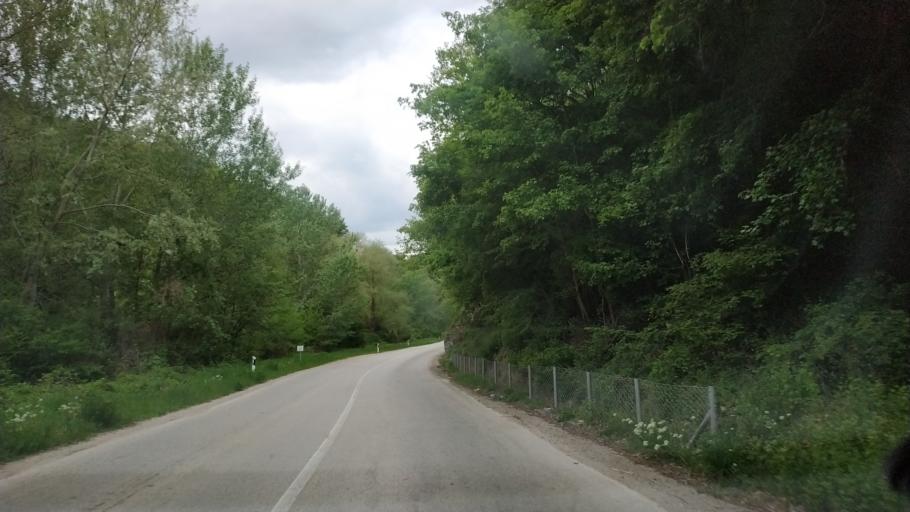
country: RS
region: Central Serbia
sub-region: Nisavski Okrug
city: Aleksinac
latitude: 43.6249
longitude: 21.7062
